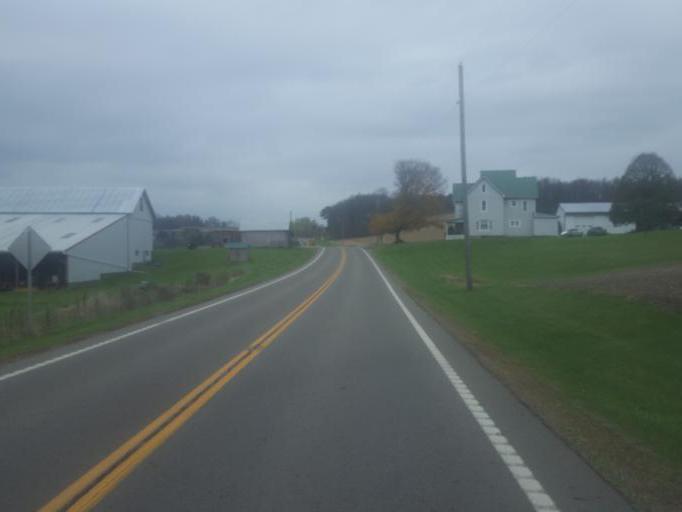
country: US
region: Ohio
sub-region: Ashland County
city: Loudonville
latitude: 40.6989
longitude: -82.2432
